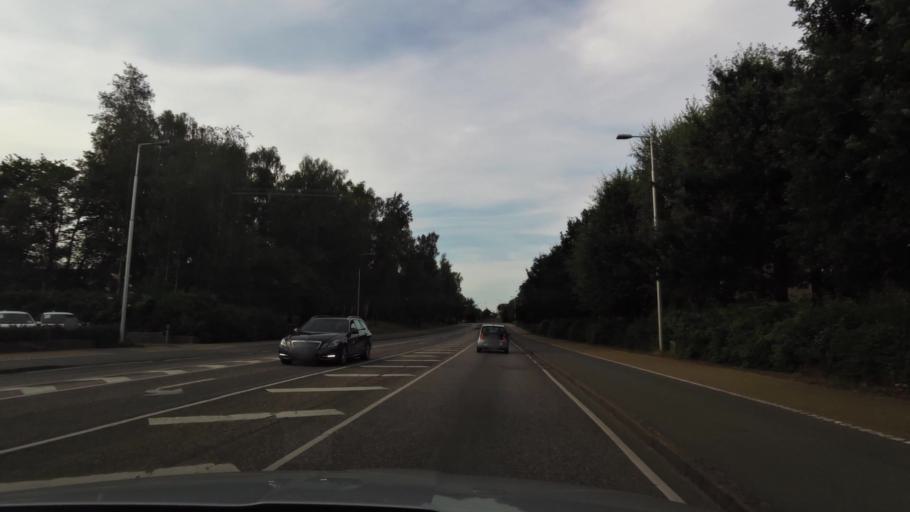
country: DK
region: Capital Region
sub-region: Rudersdal Kommune
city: Birkerod
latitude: 55.8275
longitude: 12.4301
